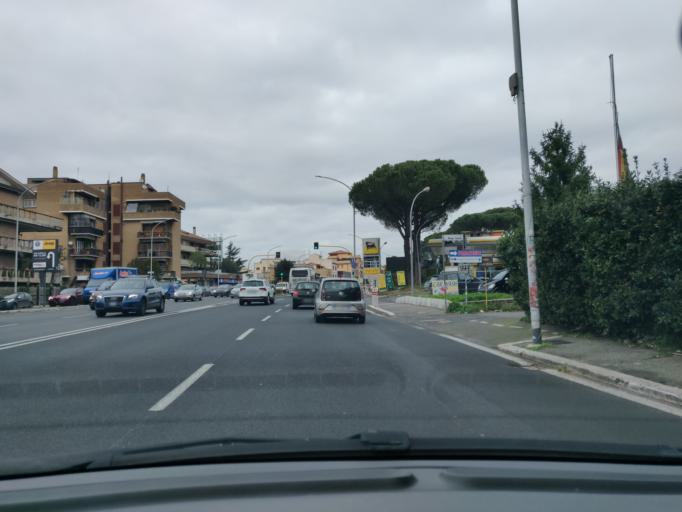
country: VA
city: Vatican City
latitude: 41.8918
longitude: 12.4137
